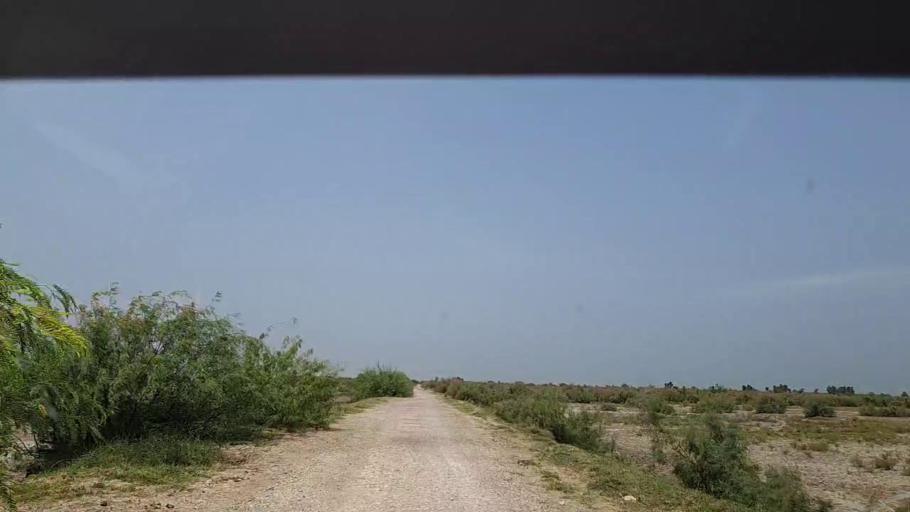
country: PK
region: Sindh
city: Adilpur
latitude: 27.8885
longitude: 69.2548
